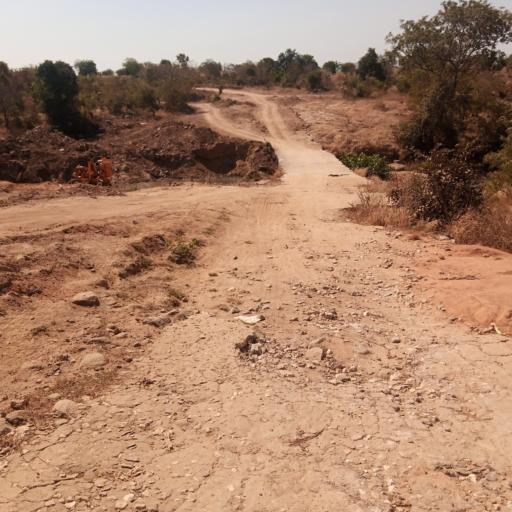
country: NG
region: Adamawa
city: Yola
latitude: 9.0060
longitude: 12.3911
